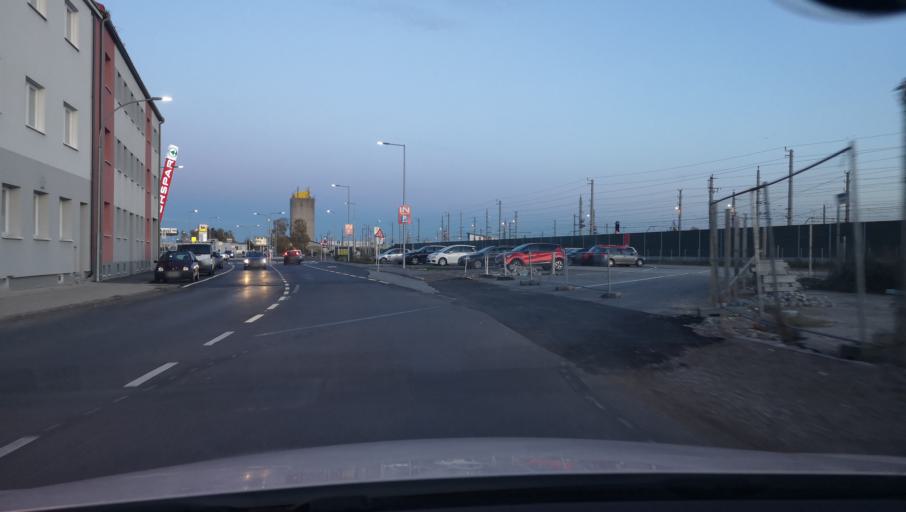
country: AT
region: Lower Austria
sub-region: Politischer Bezirk Amstetten
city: Amstetten
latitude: 48.1224
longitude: 14.8848
